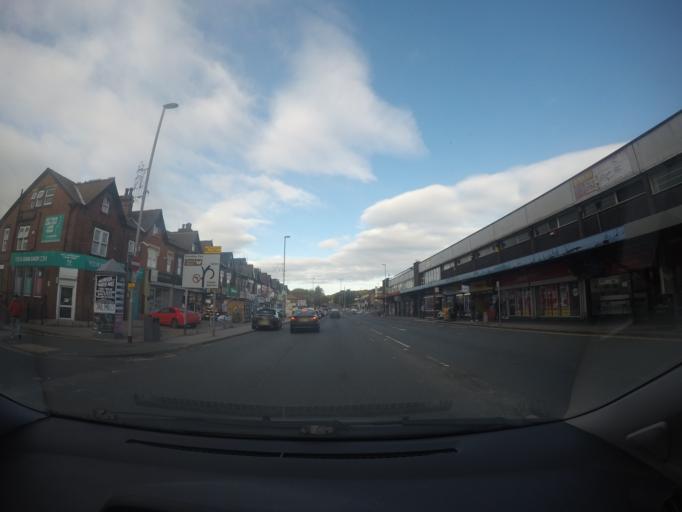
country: GB
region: England
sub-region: City and Borough of Leeds
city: Chapel Allerton
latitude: 53.8171
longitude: -1.5169
